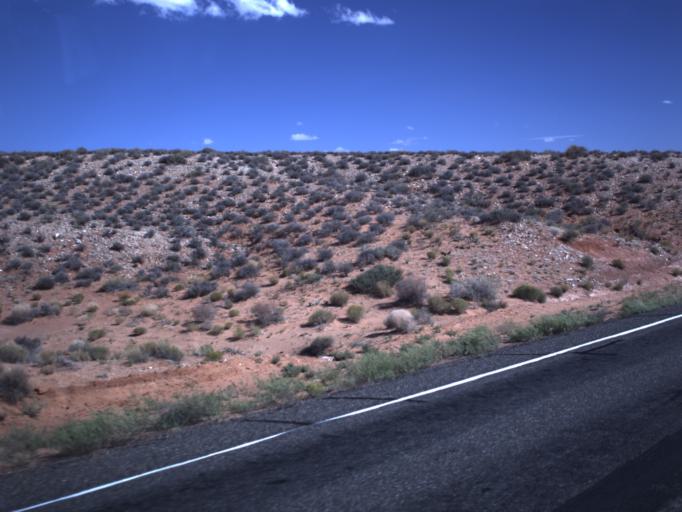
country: US
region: Utah
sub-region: Wayne County
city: Loa
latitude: 38.0752
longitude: -110.6093
